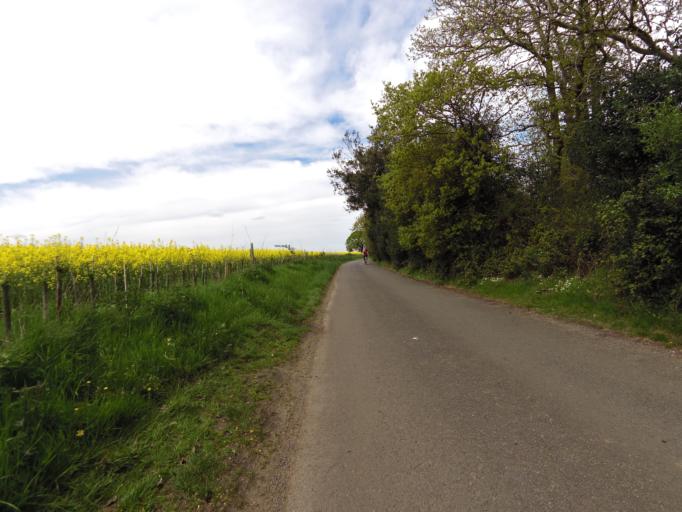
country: GB
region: England
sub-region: Essex
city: Mistley
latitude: 51.9918
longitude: 1.1320
